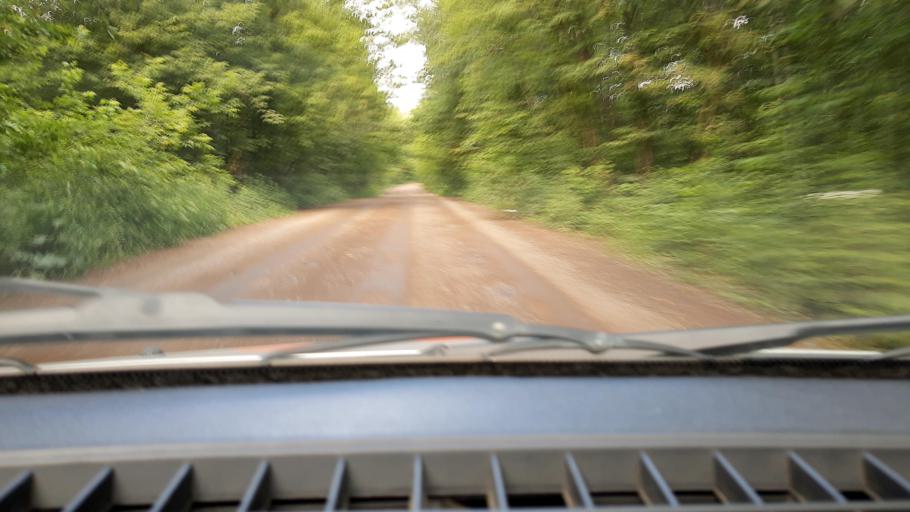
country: RU
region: Bashkortostan
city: Ufa
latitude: 54.6769
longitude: 56.0634
